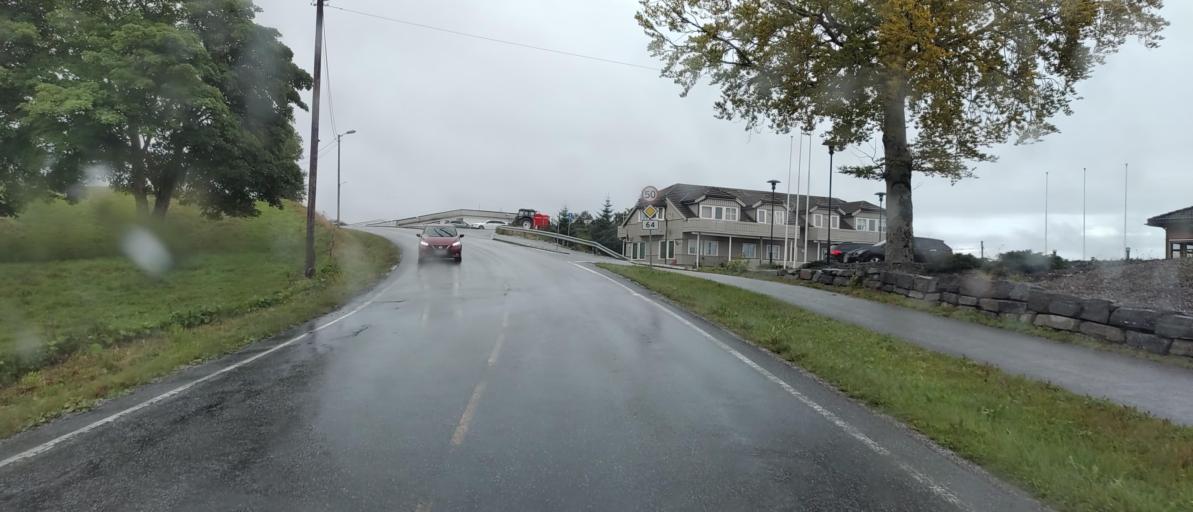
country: NO
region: More og Romsdal
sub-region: Eide
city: Eide
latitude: 63.0165
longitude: 7.4533
